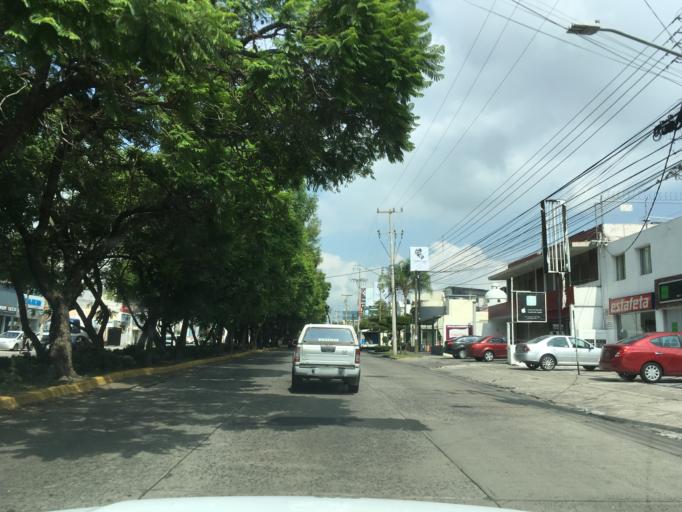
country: MX
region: Jalisco
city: Guadalajara
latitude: 20.6667
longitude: -103.3866
